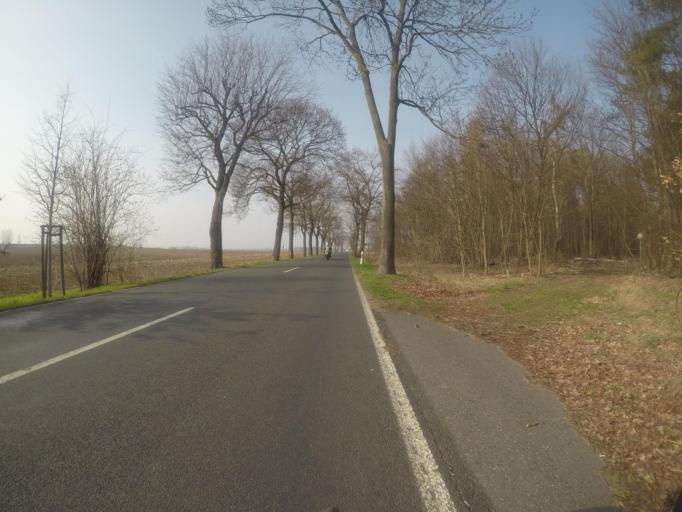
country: DE
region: Brandenburg
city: Schonefeld
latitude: 52.3428
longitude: 13.4872
